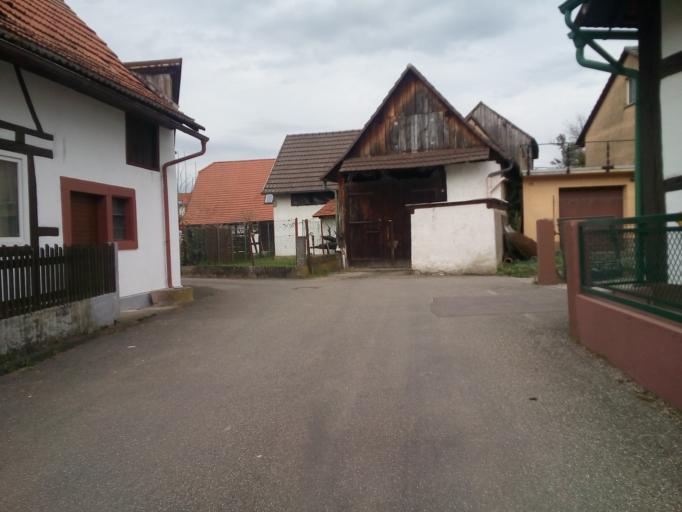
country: DE
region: Baden-Wuerttemberg
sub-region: Freiburg Region
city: Rheinau
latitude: 48.6537
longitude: 7.9229
